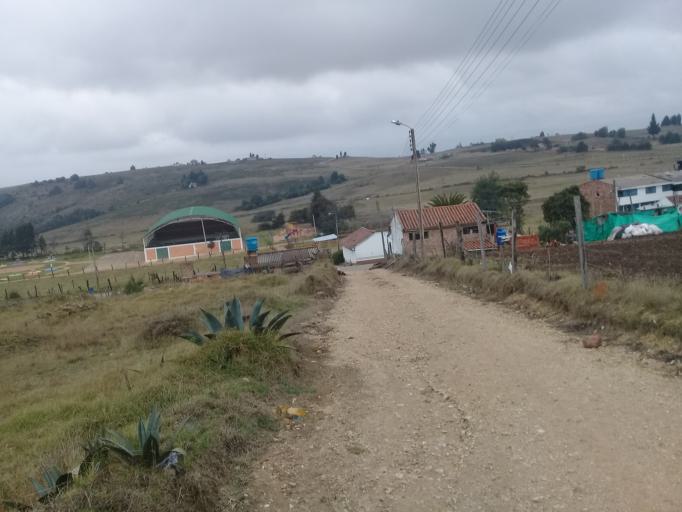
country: CO
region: Boyaca
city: Siachoque
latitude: 5.5600
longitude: -73.2813
